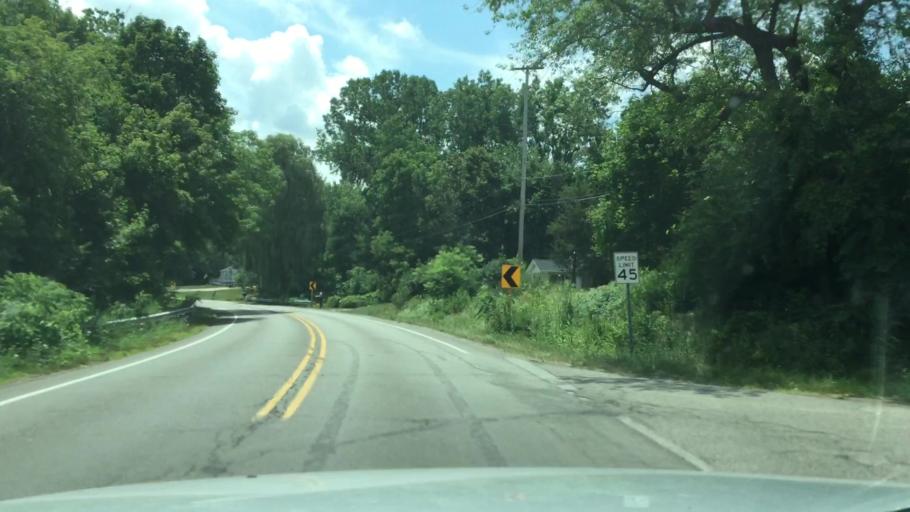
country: US
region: Michigan
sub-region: Genesee County
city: Flushing
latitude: 43.0741
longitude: -83.8729
